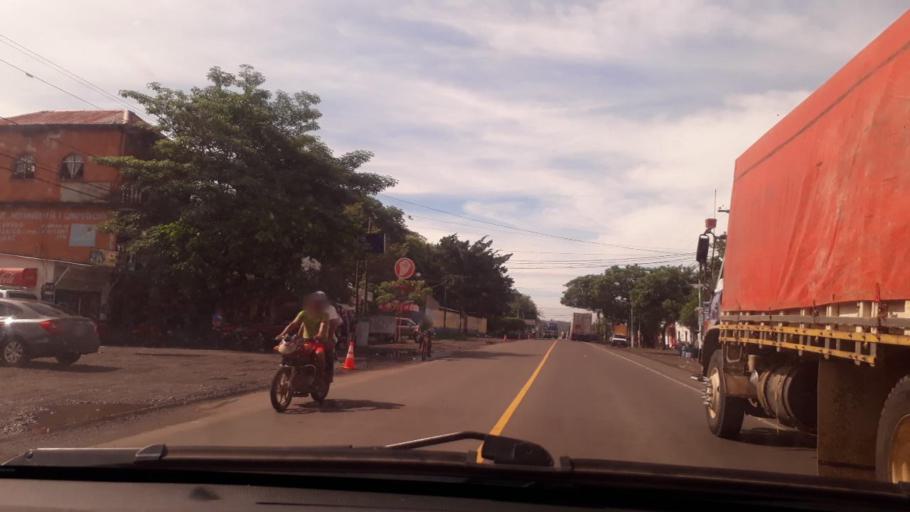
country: SV
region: Ahuachapan
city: San Francisco Menendez
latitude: 13.8733
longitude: -90.0959
